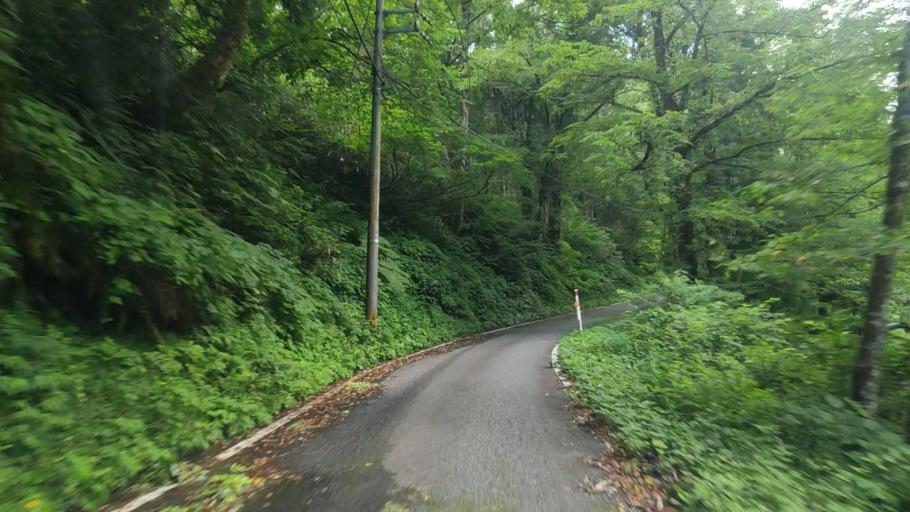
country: JP
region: Fukui
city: Katsuyama
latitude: 36.1997
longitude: 136.5253
